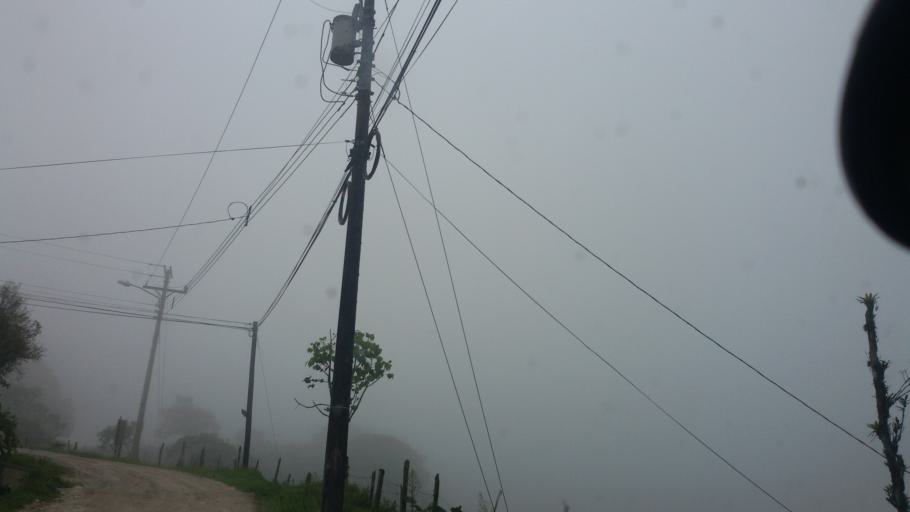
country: CR
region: San Jose
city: Ipis
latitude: 10.0211
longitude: -83.9483
